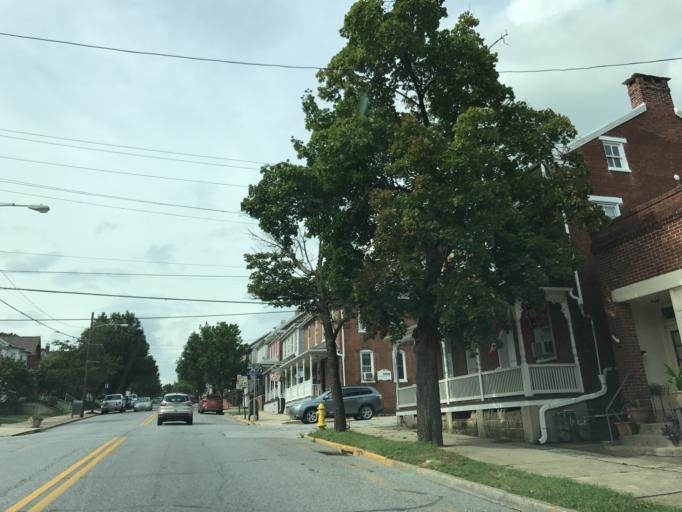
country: US
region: Pennsylvania
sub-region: York County
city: Spring Grove
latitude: 39.8743
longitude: -76.8655
